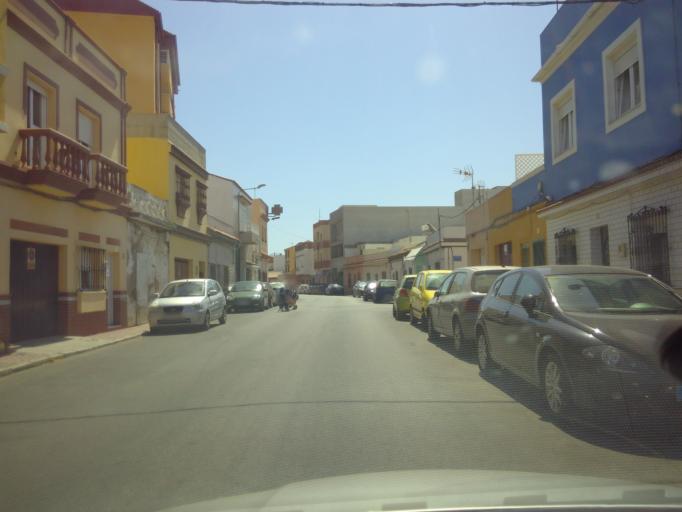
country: ES
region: Andalusia
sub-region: Provincia de Cadiz
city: La Linea de la Concepcion
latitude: 36.1673
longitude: -5.3463
